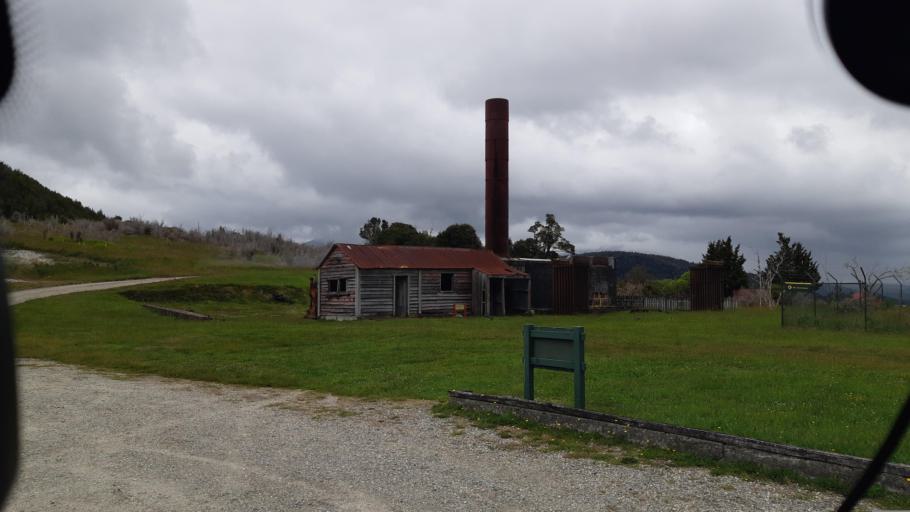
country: NZ
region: West Coast
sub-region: Buller District
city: Westport
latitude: -42.2944
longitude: 171.8245
